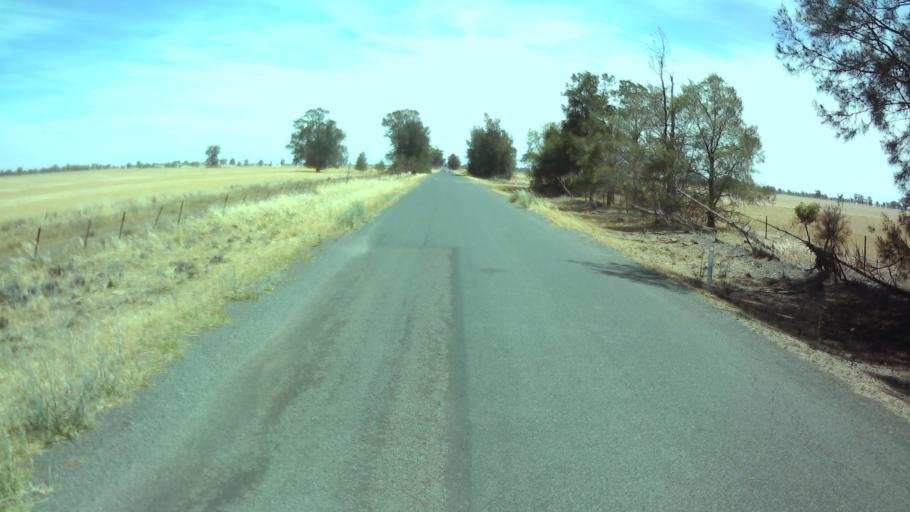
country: AU
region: New South Wales
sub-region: Weddin
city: Grenfell
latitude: -33.9231
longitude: 147.7637
